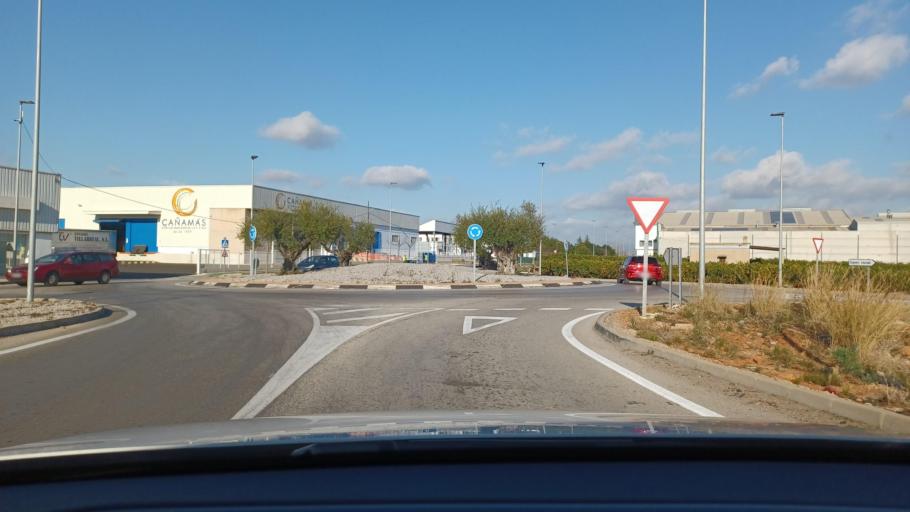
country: ES
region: Valencia
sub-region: Provincia de Castello
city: Betxi
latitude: 39.9316
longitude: -0.1949
